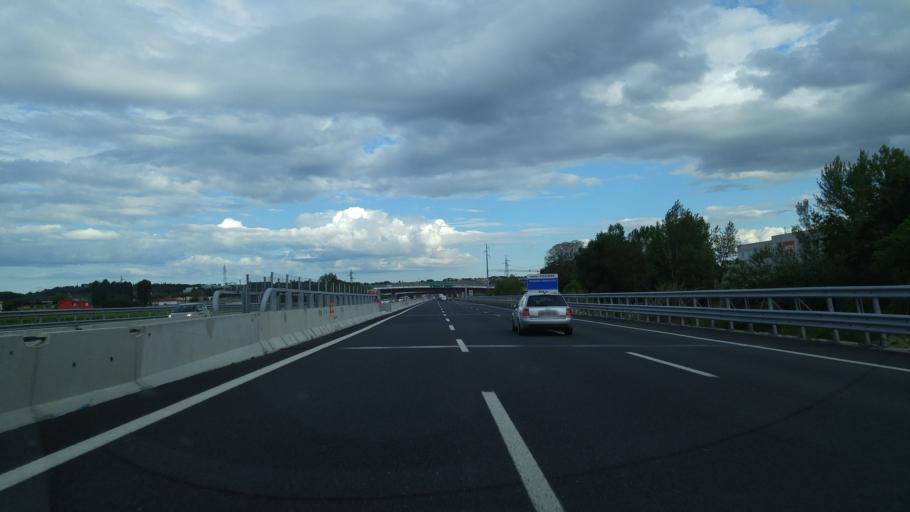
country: IT
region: Emilia-Romagna
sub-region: Provincia di Rimini
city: Riccione
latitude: 43.9895
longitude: 12.6301
